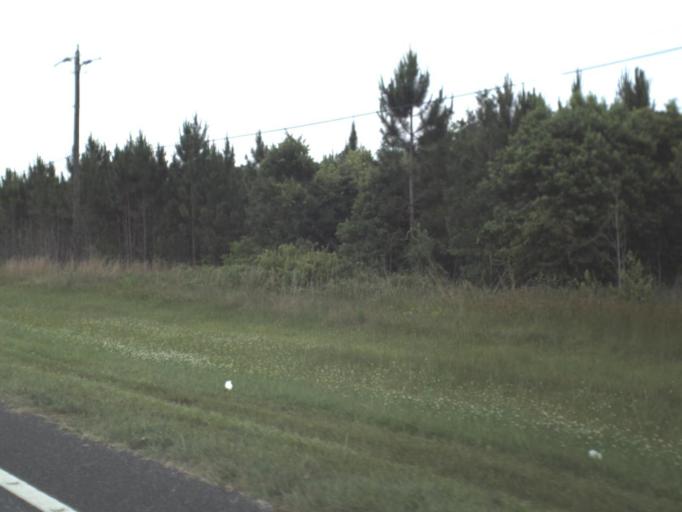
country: US
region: Florida
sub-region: Putnam County
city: Palatka
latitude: 29.6805
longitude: -81.6608
